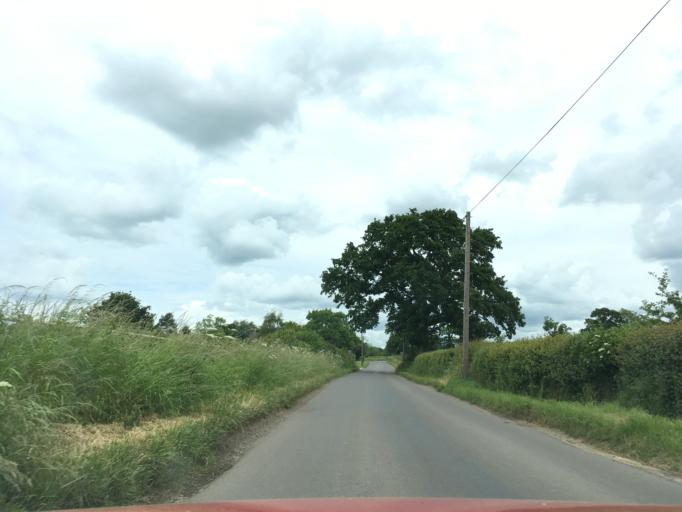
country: GB
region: England
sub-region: Wiltshire
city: Charlton
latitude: 51.5506
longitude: -2.0509
